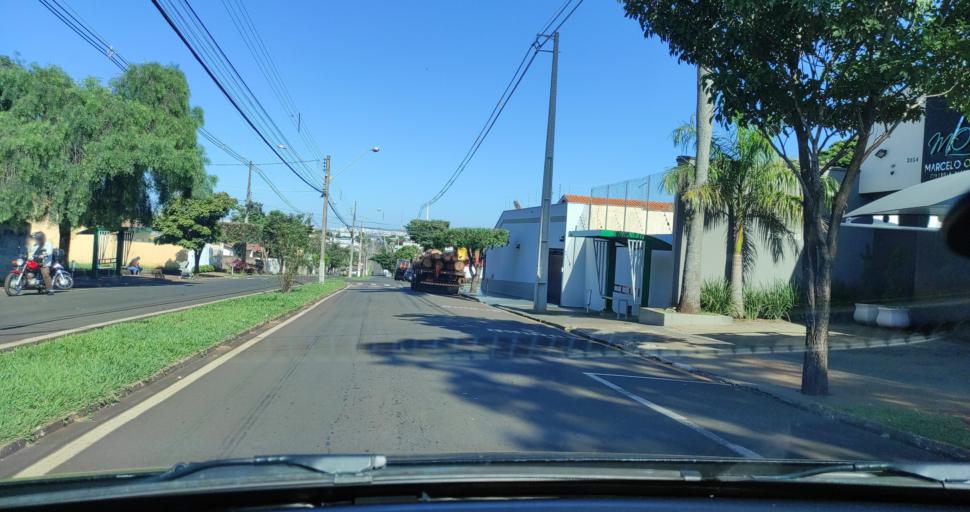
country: BR
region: Parana
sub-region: Ibipora
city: Ibipora
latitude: -23.2724
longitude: -51.0629
